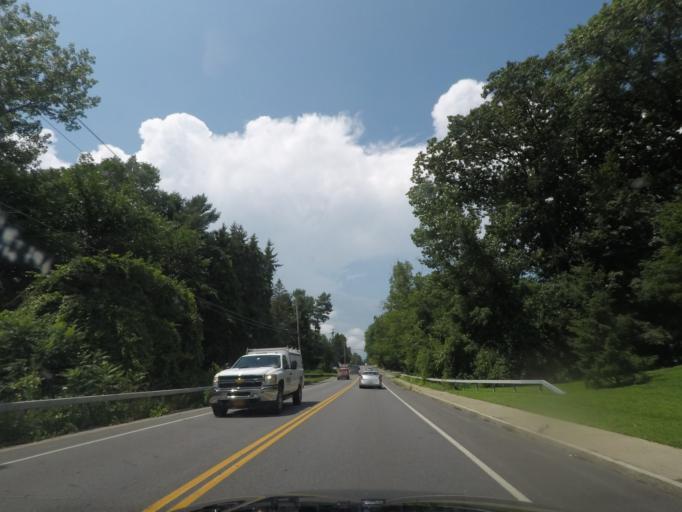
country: US
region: New York
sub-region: Albany County
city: West Albany
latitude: 42.7094
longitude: -73.7796
